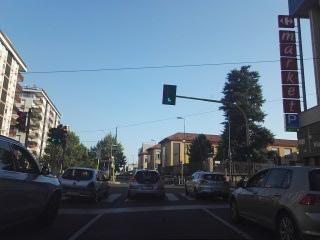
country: IT
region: Lombardy
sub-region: Citta metropolitana di Milano
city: Romano Banco
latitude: 45.4663
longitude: 9.1463
